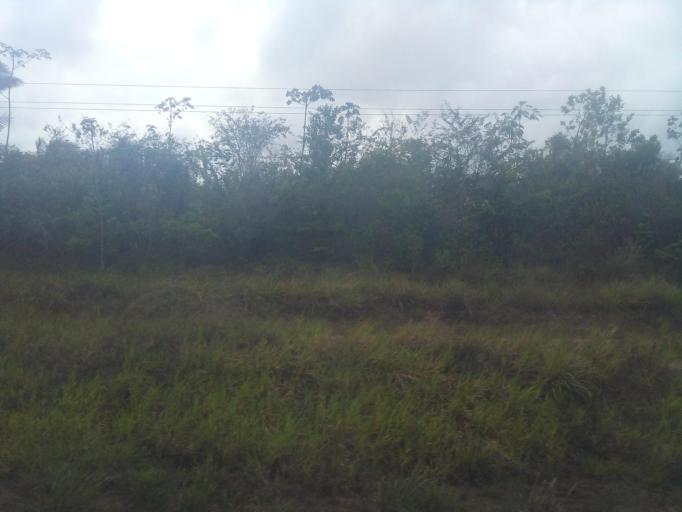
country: BR
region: Maranhao
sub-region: Itapecuru Mirim
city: Itapecuru Mirim
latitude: -3.1709
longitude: -44.3627
